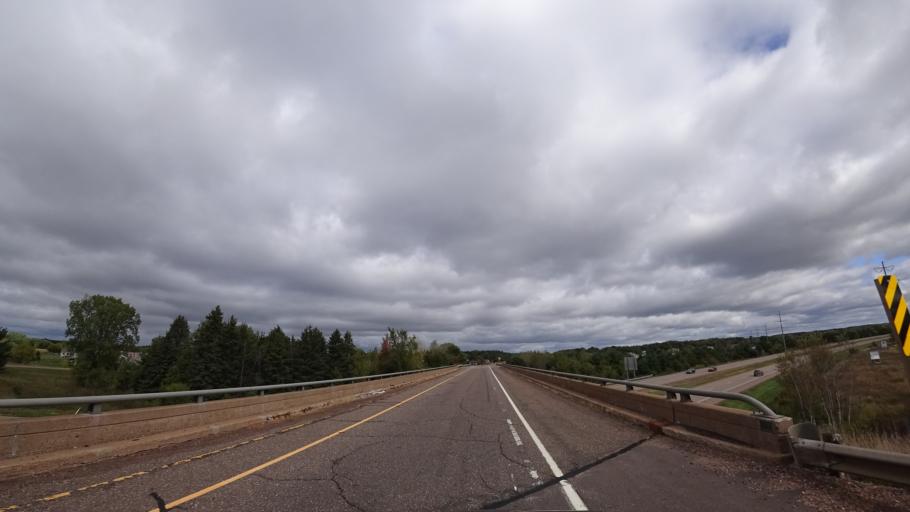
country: US
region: Wisconsin
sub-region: Chippewa County
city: Lake Wissota
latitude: 44.9193
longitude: -91.3374
